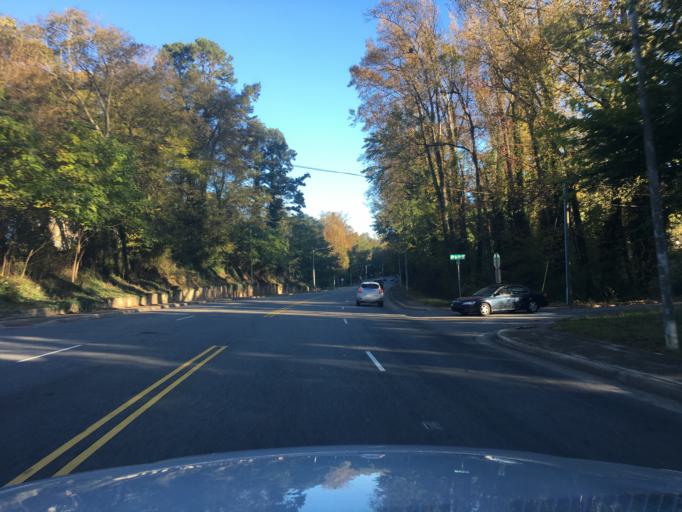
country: US
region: North Carolina
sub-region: Catawba County
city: Hickory
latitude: 35.7229
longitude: -81.3365
